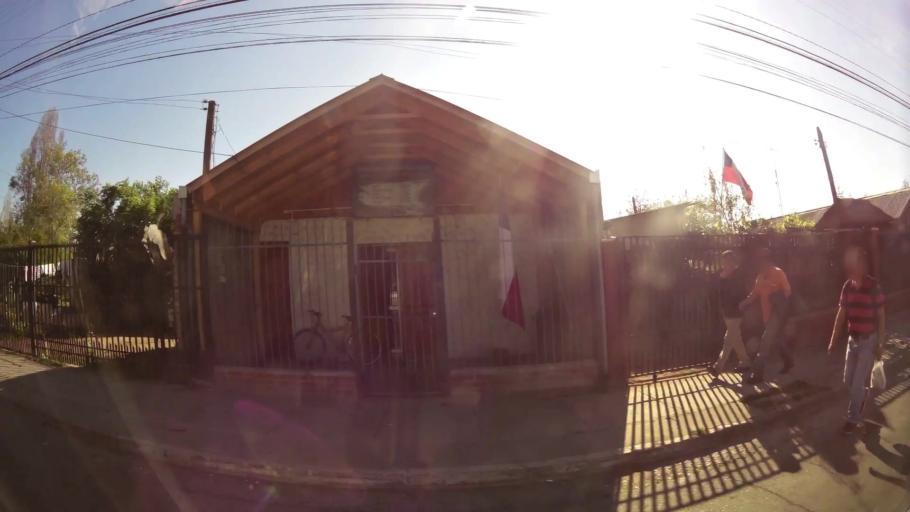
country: CL
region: Santiago Metropolitan
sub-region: Provincia de Talagante
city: Penaflor
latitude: -33.6115
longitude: -70.8720
